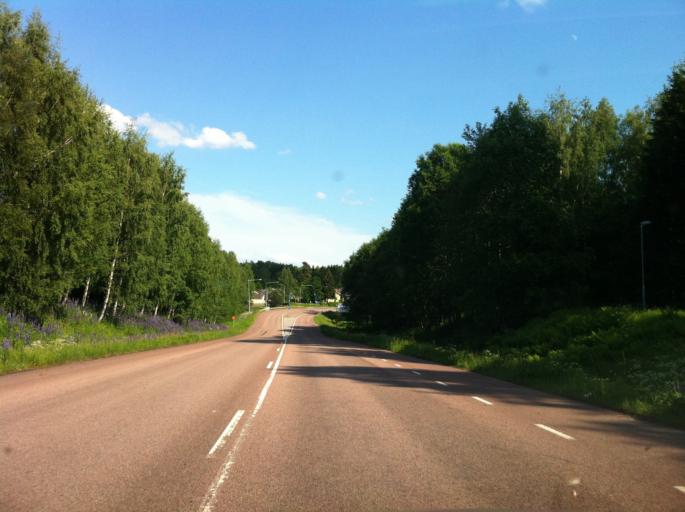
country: SE
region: Vaermland
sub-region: Kils Kommun
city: Kil
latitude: 59.5229
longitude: 13.3073
